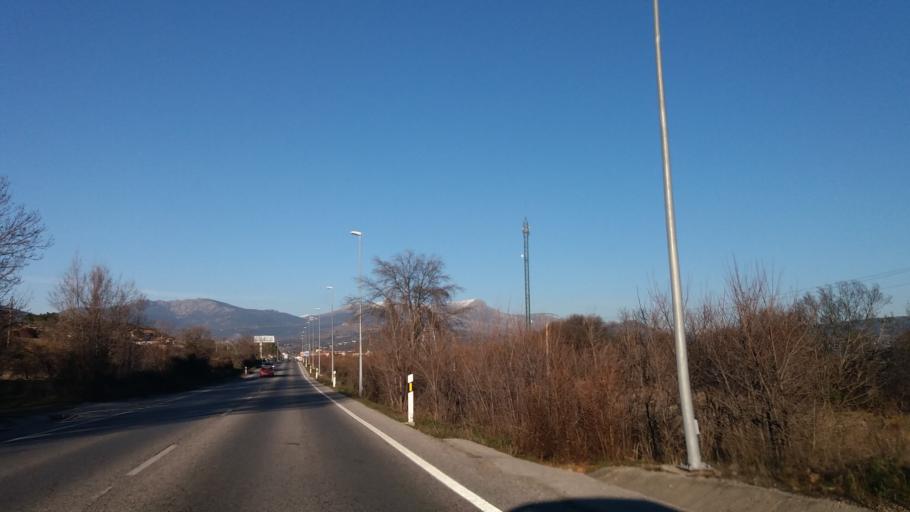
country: ES
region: Madrid
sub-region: Provincia de Madrid
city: Guadarrama
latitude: 40.6587
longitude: -4.0944
